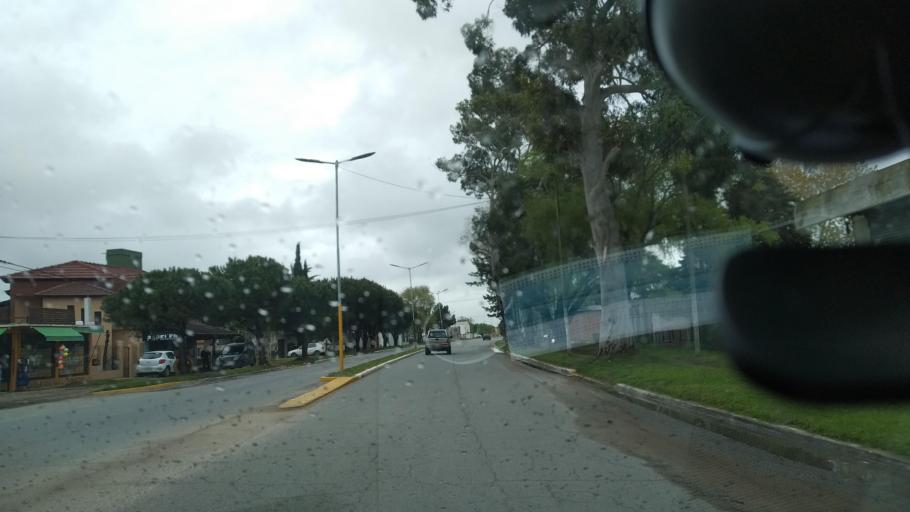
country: AR
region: Buenos Aires
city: San Clemente del Tuyu
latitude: -36.3816
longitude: -56.7222
